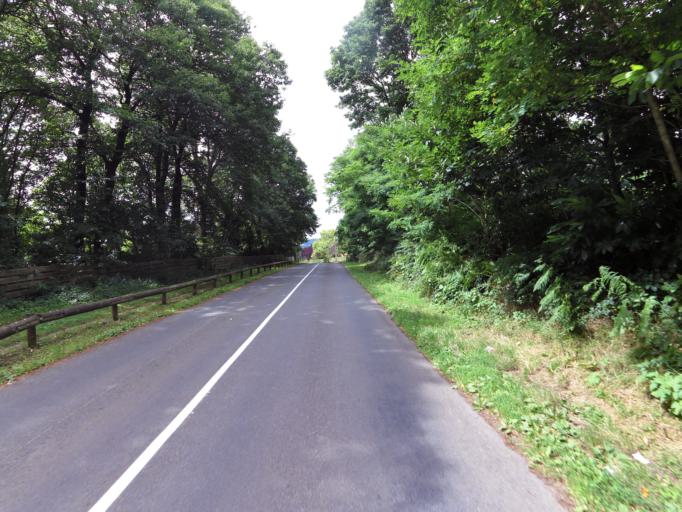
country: FR
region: Nord-Pas-de-Calais
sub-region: Departement du Nord
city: Saint-Jans-Cappel
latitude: 50.7803
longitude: 2.7273
